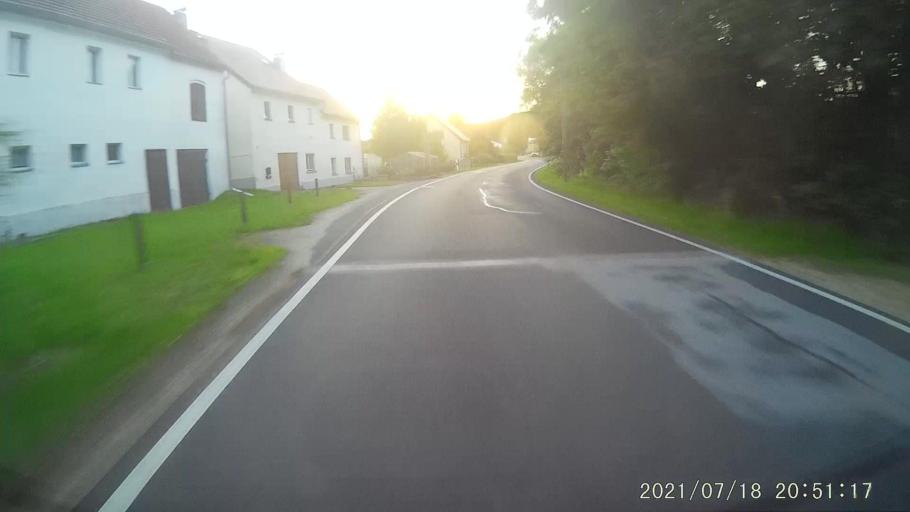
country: DE
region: Saxony
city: Konigshain
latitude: 51.1839
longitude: 14.8530
